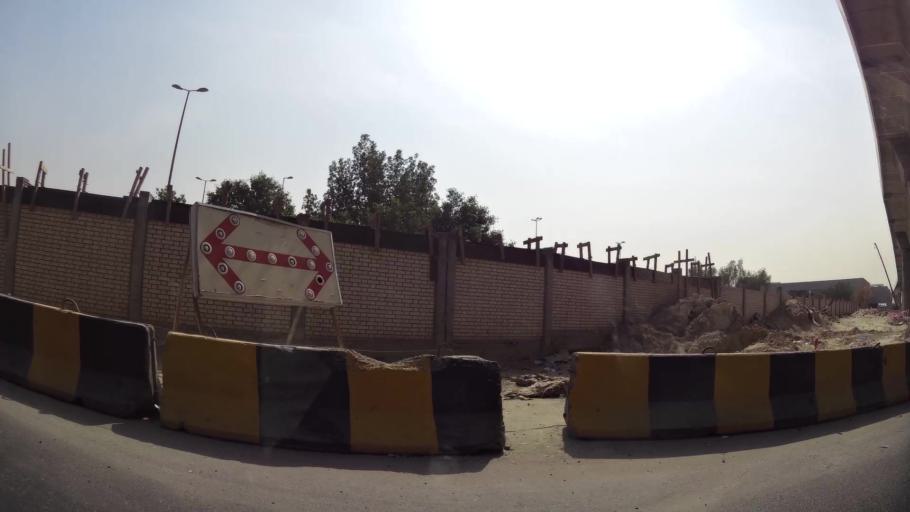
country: KW
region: Al Asimah
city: Ash Shamiyah
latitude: 29.3345
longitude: 47.9354
